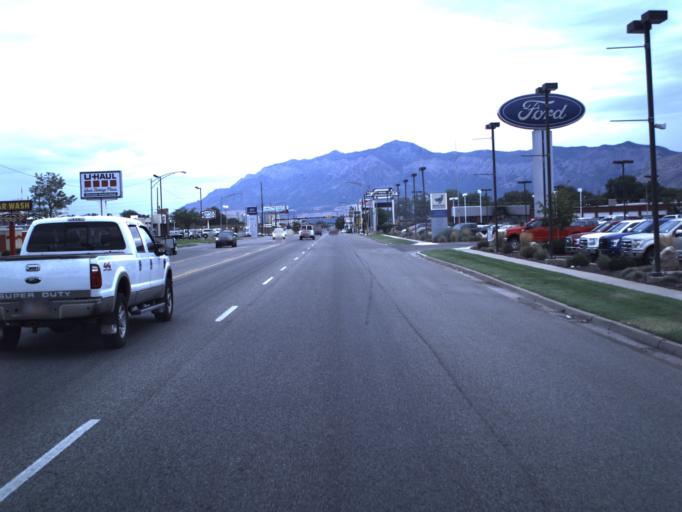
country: US
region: Utah
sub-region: Weber County
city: South Ogden
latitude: 41.2002
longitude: -111.9793
